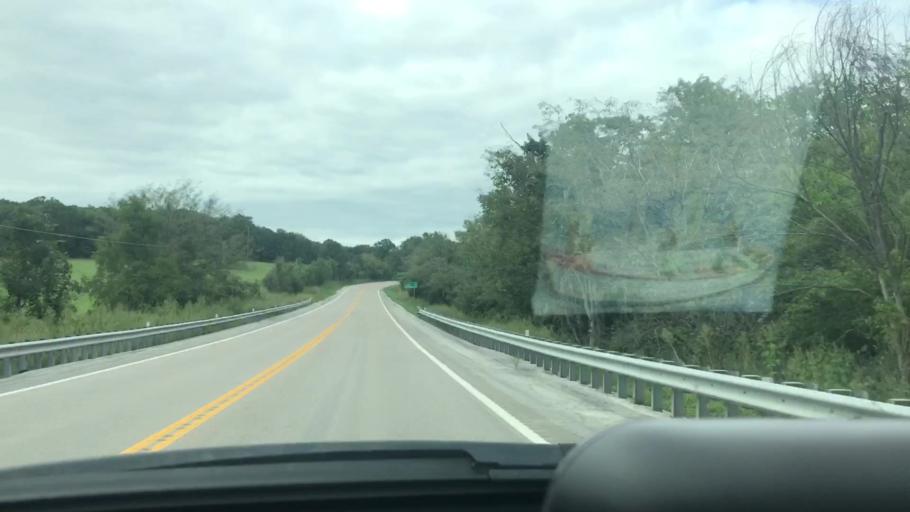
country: US
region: Missouri
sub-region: Benton County
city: Warsaw
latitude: 38.1230
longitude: -93.2788
